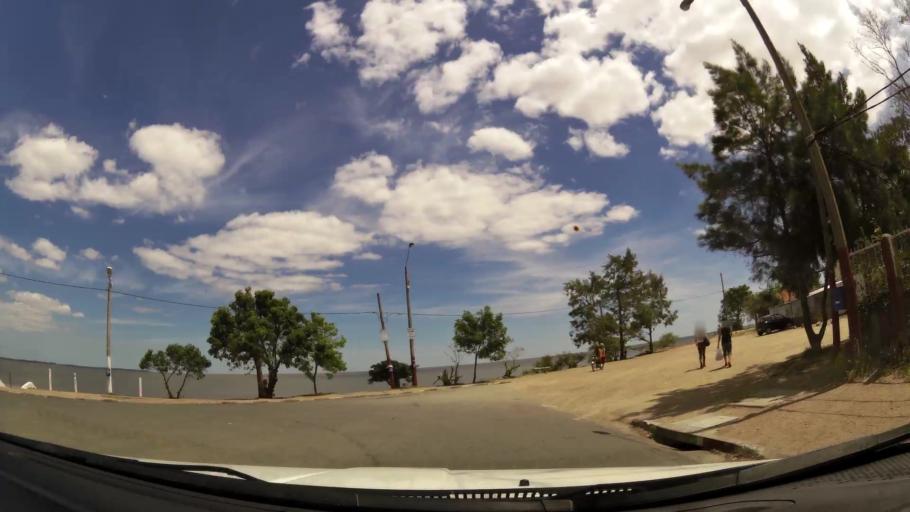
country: UY
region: San Jose
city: Delta del Tigre
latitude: -34.7509
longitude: -56.4559
